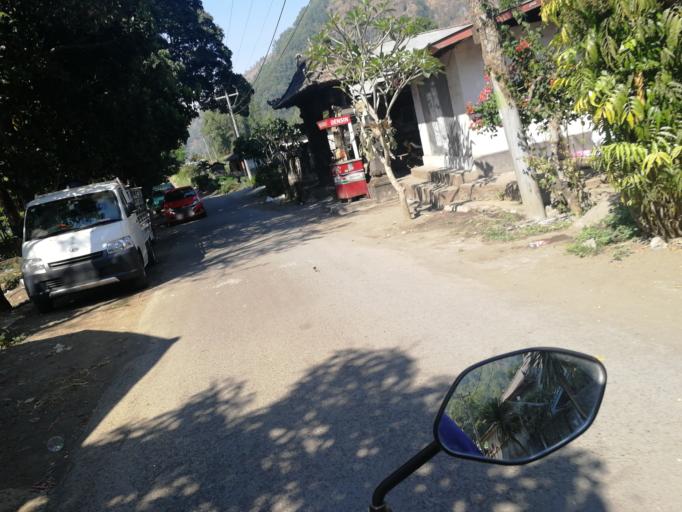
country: ID
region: Bali
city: Banjar Buahan
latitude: -8.2795
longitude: 115.4111
